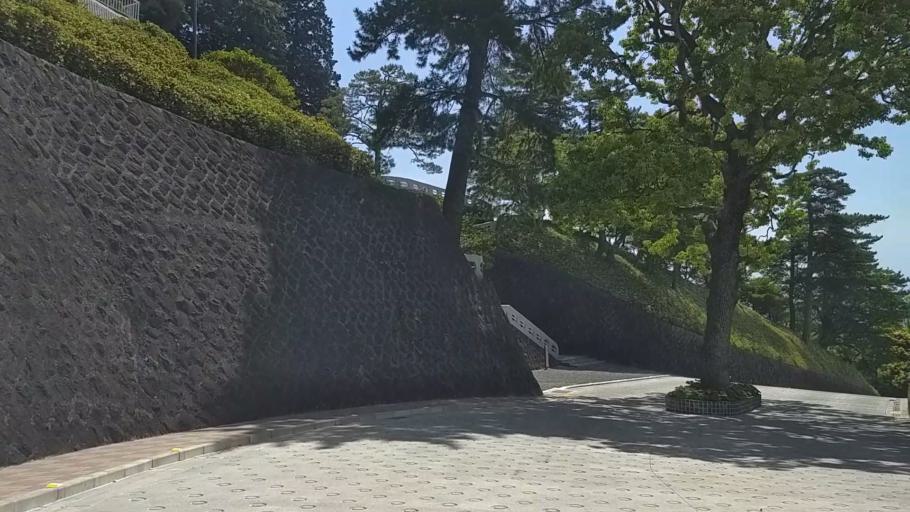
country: JP
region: Shizuoka
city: Atami
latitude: 35.1087
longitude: 139.0784
